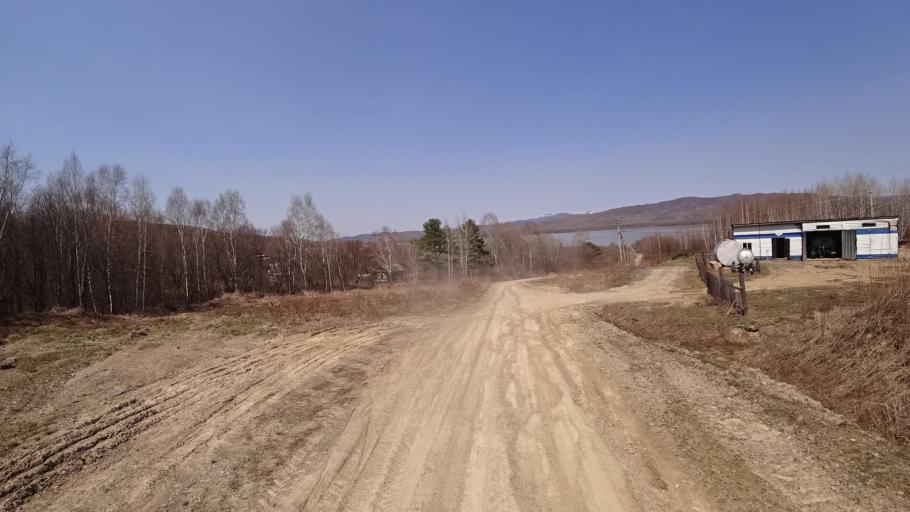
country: RU
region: Khabarovsk Krai
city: Selikhino
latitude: 50.6645
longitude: 137.4044
